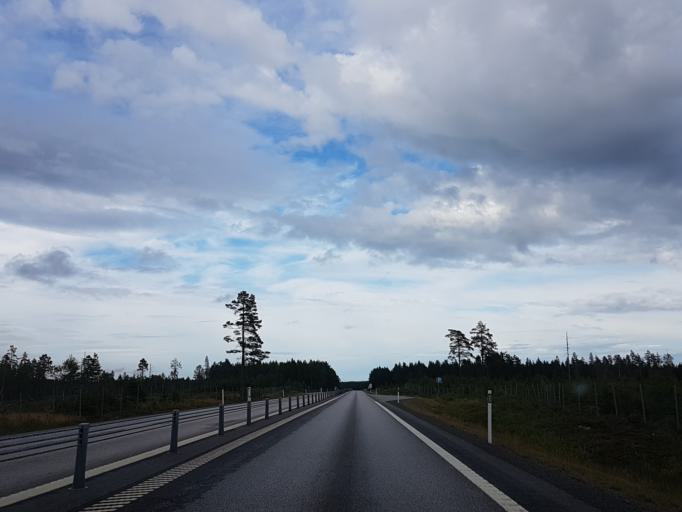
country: SE
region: Vaesterbotten
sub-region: Umea Kommun
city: Saevar
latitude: 63.9216
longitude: 20.6118
